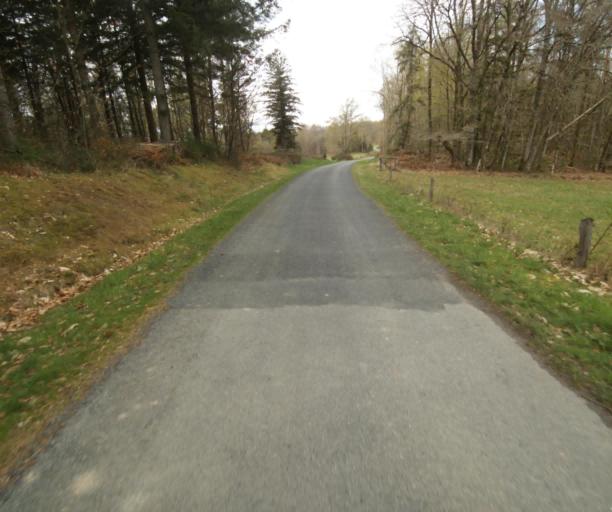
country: FR
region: Limousin
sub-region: Departement de la Correze
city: Argentat
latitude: 45.1908
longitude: 1.9273
